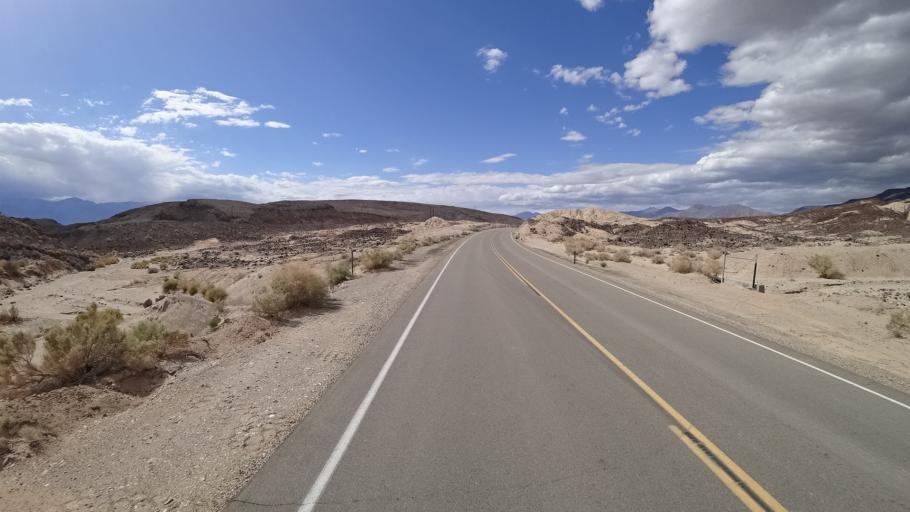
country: US
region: California
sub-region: Inyo County
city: Lone Pine
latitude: 36.3772
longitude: -117.8025
